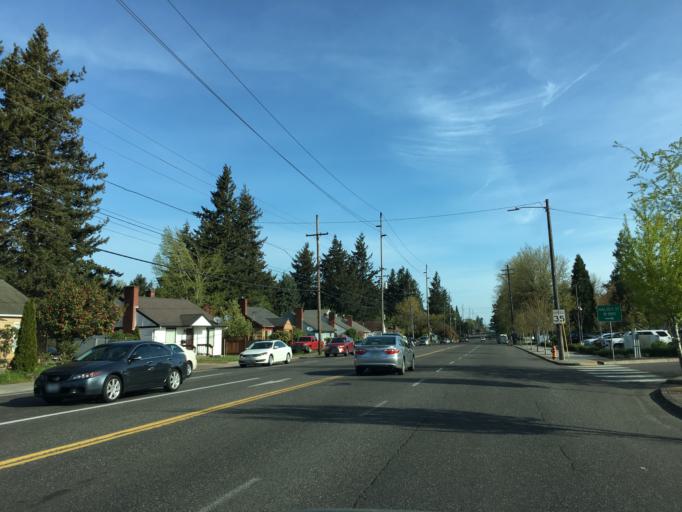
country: US
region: Oregon
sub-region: Multnomah County
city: Lents
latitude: 45.5343
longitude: -122.5579
